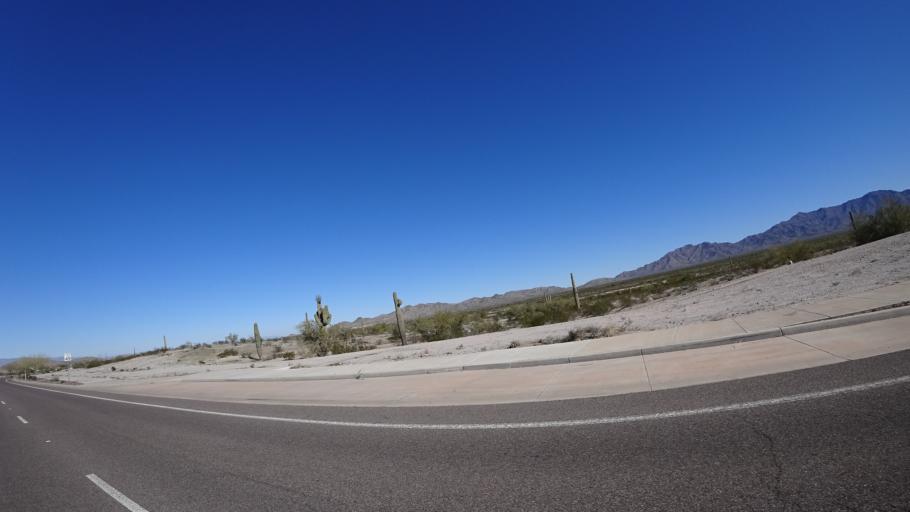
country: US
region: Arizona
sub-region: Maricopa County
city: Goodyear
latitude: 33.3078
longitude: -112.4326
